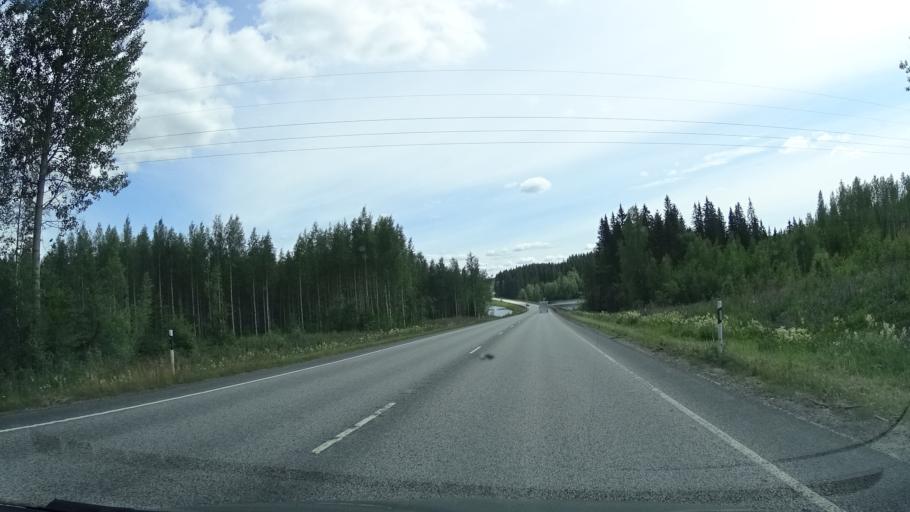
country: FI
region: Central Finland
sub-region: Jyvaeskylae
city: Jyvaeskylae
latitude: 62.2589
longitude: 25.6078
